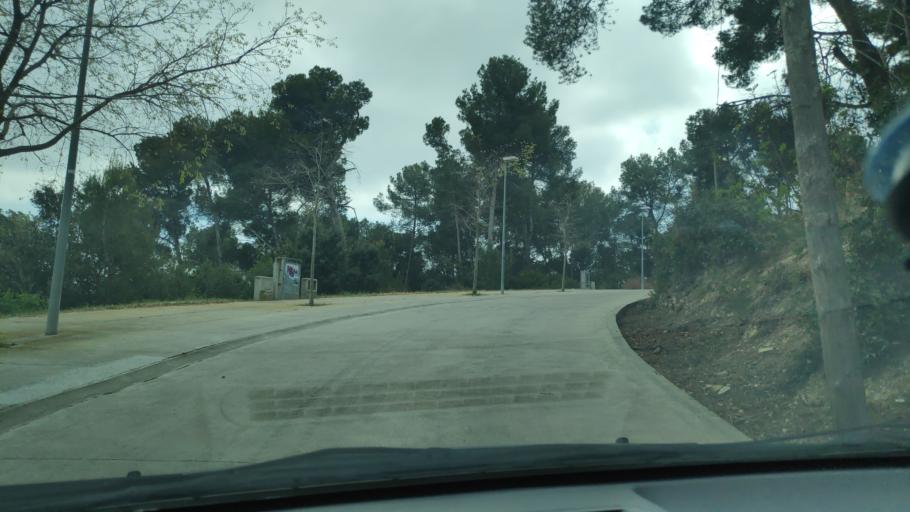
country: ES
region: Catalonia
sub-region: Provincia de Barcelona
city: Sant Quirze del Valles
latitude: 41.5153
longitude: 2.0902
